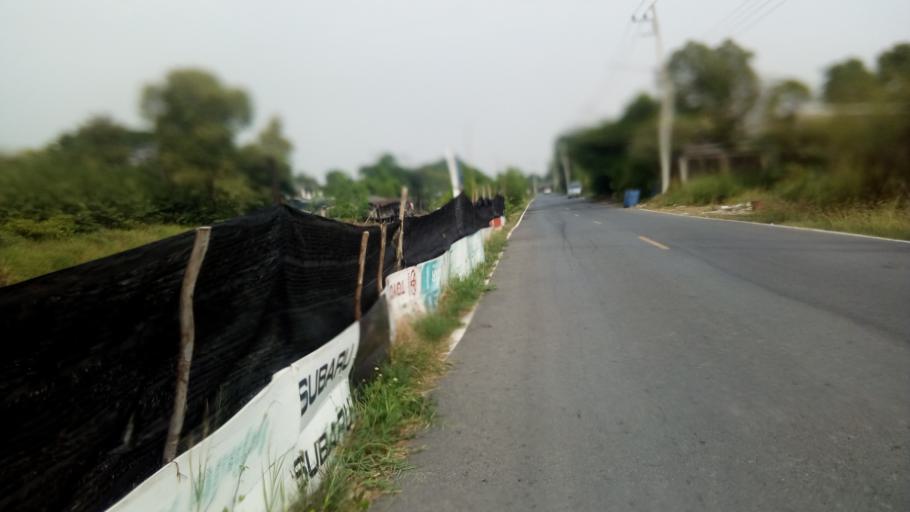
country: TH
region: Pathum Thani
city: Nong Suea
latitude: 14.0572
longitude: 100.8468
